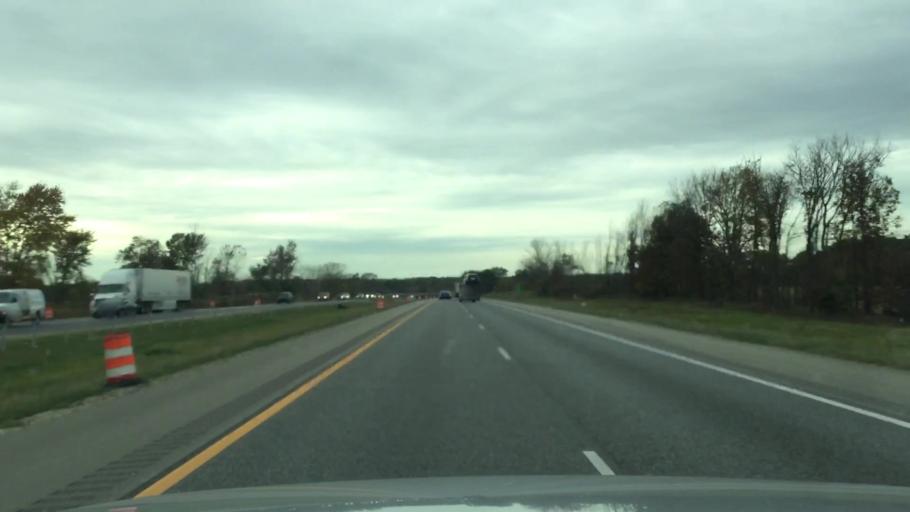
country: US
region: Michigan
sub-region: Van Buren County
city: Decatur
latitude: 42.1939
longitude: -86.0219
